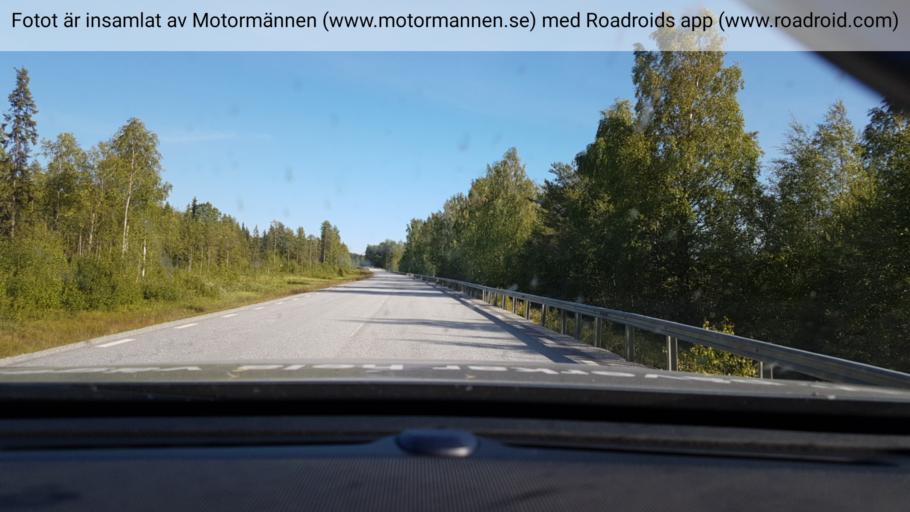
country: SE
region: Vaesterbotten
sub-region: Vindelns Kommun
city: Vindeln
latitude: 64.1896
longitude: 19.4637
